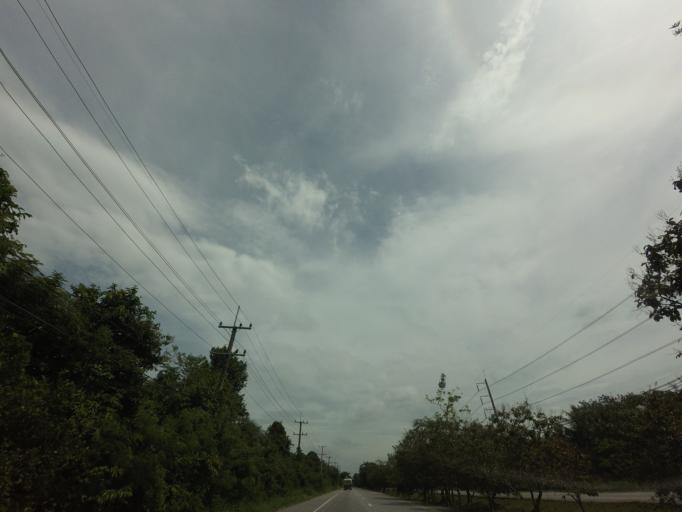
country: TH
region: Rayong
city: Klaeng
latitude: 12.7040
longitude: 101.5455
